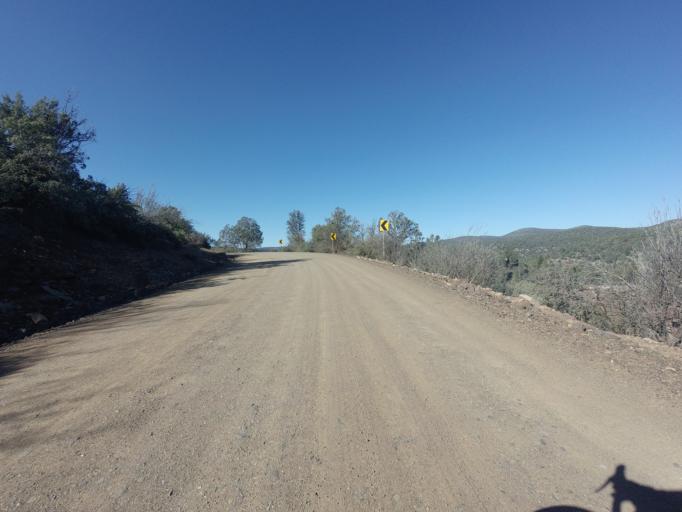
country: US
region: Arizona
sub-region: Gila County
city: Payson
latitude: 34.2976
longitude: -111.3542
